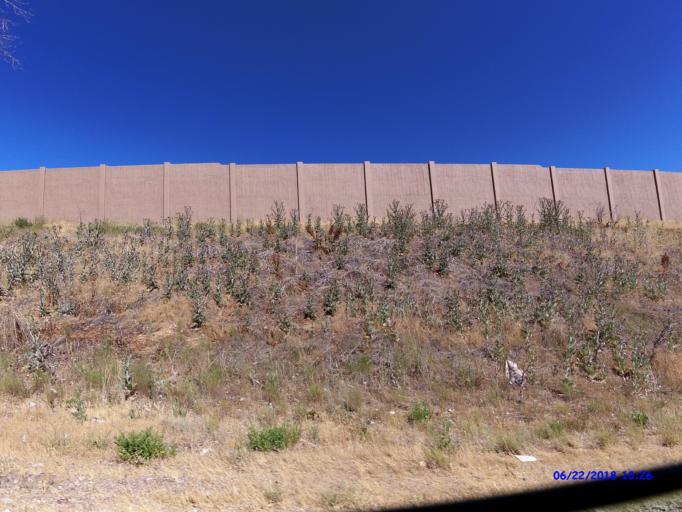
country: US
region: Utah
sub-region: Weber County
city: Riverdale
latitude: 41.1965
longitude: -111.9987
